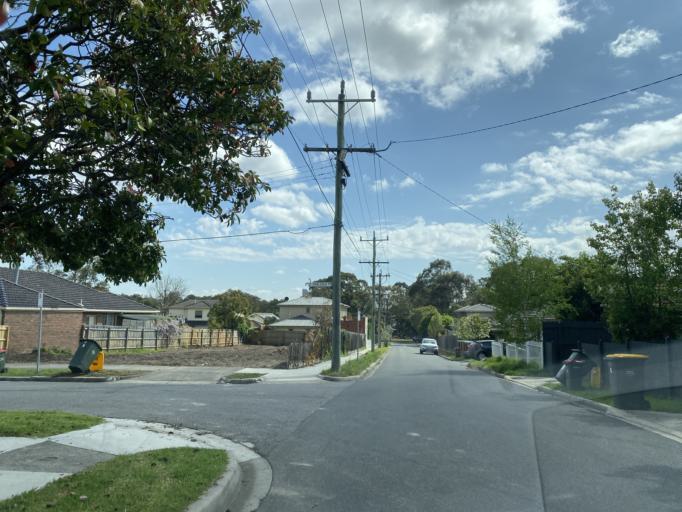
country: AU
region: Victoria
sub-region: Whitehorse
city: Burwood
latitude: -37.8460
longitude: 145.1244
